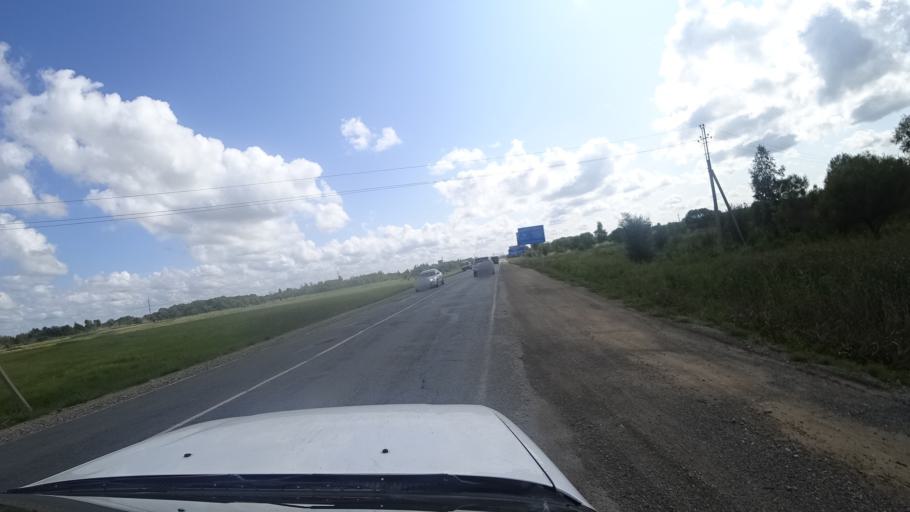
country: RU
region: Primorskiy
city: Dal'nerechensk
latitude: 45.9238
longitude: 133.7736
